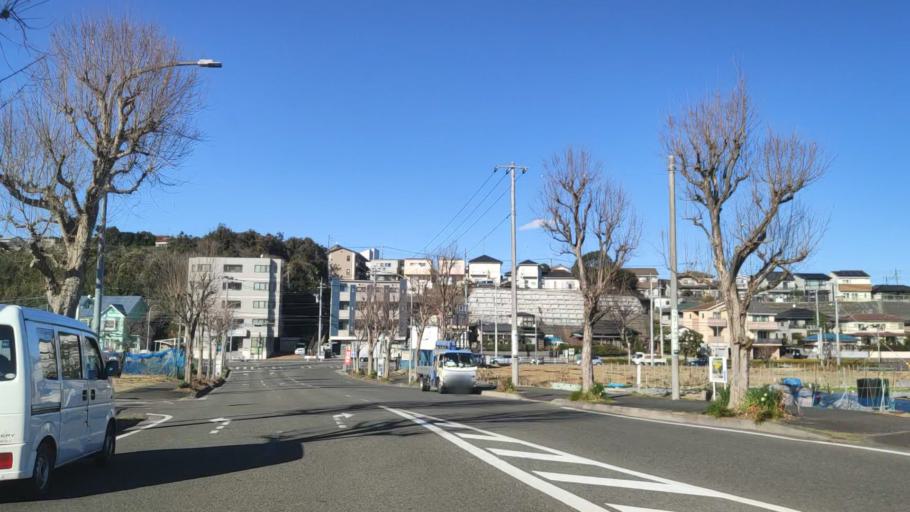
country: JP
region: Tokyo
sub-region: Machida-shi
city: Machida
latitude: 35.5175
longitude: 139.5416
